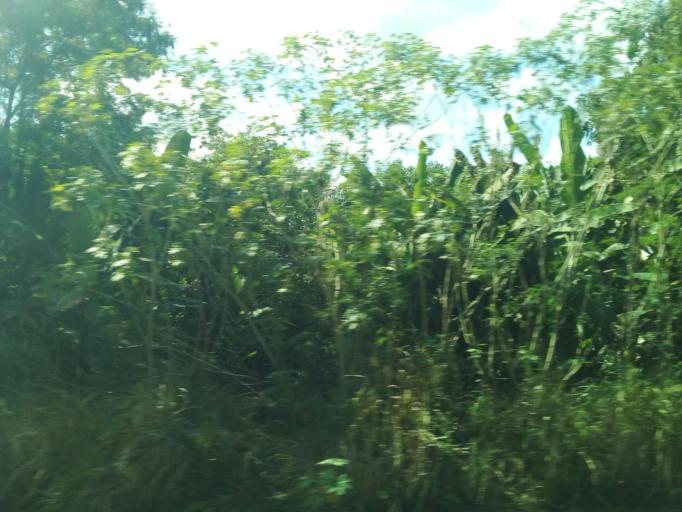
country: BR
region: Minas Gerais
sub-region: Governador Valadares
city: Governador Valadares
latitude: -18.8723
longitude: -41.7798
